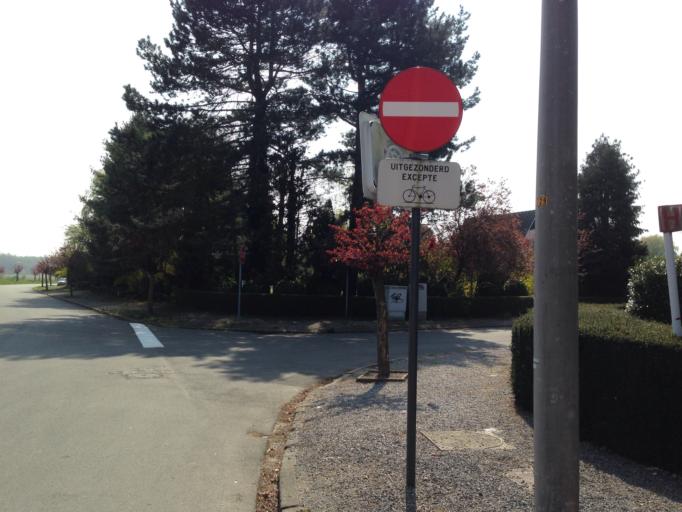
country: BE
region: Flanders
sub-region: Provincie Vlaams-Brabant
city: Wemmel
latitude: 50.9000
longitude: 4.3031
